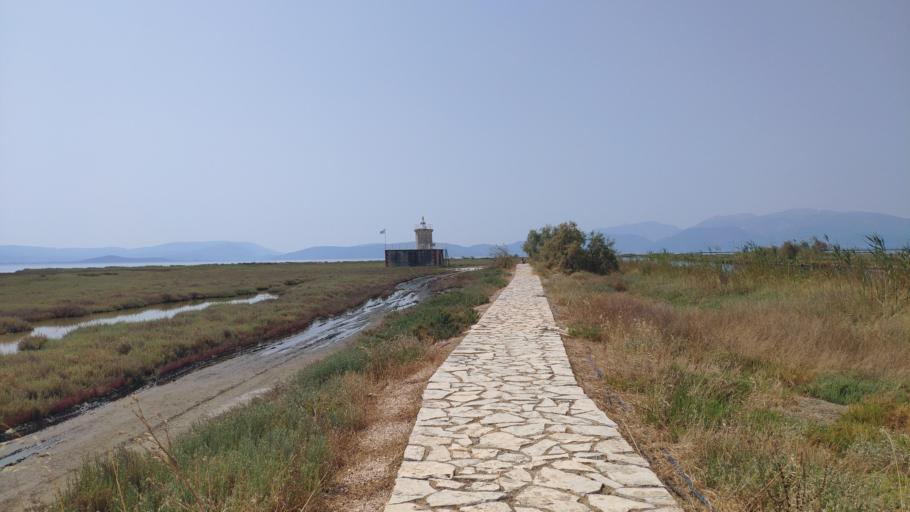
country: GR
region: West Greece
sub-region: Nomos Aitolias kai Akarnanias
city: Menidi
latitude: 39.0309
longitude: 21.0753
